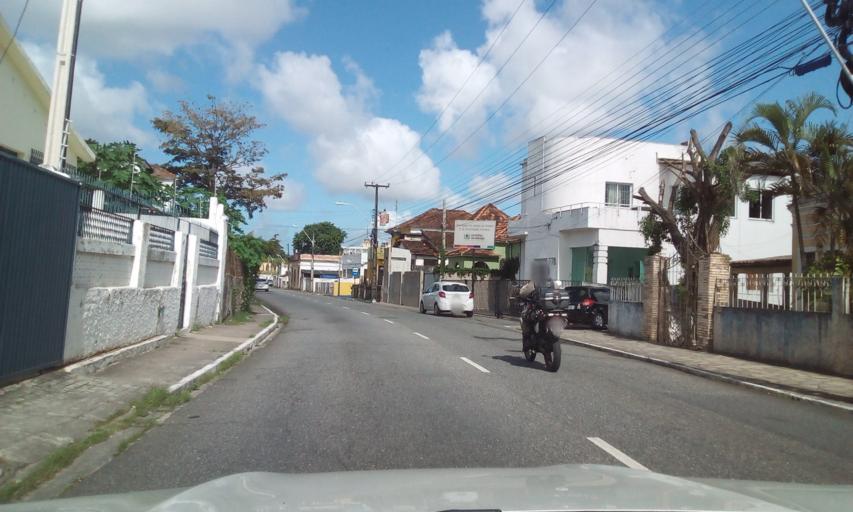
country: BR
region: Paraiba
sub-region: Joao Pessoa
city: Joao Pessoa
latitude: -7.1293
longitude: -34.8835
